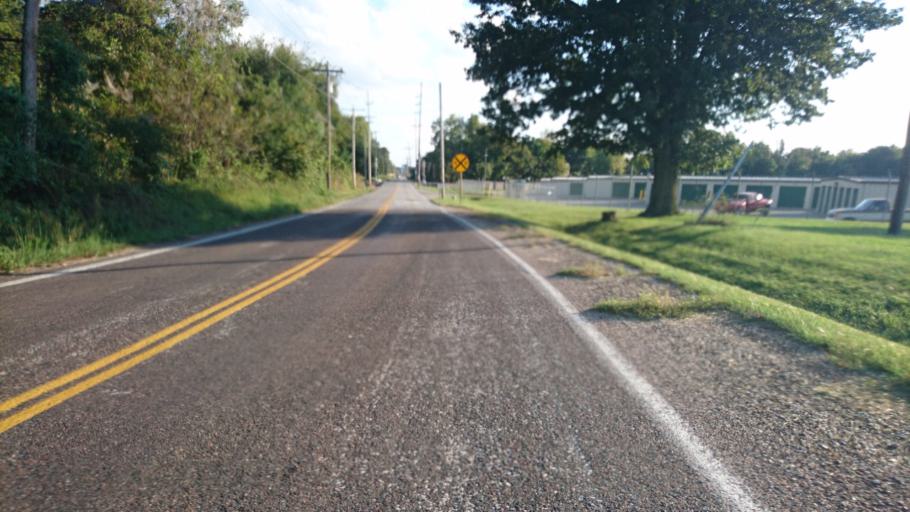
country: US
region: Missouri
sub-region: Greene County
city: Springfield
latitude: 37.2106
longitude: -93.3859
